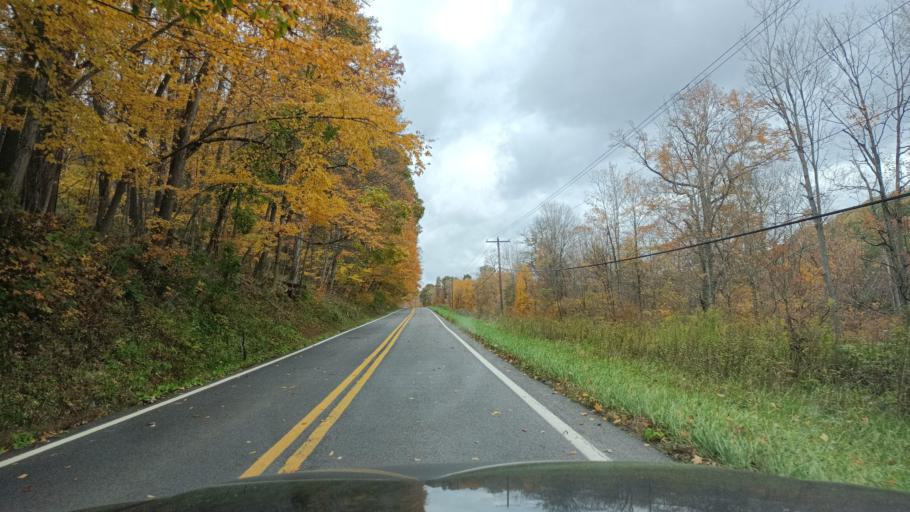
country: US
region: West Virginia
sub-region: Monongalia County
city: Cheat Lake
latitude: 39.6534
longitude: -79.7298
